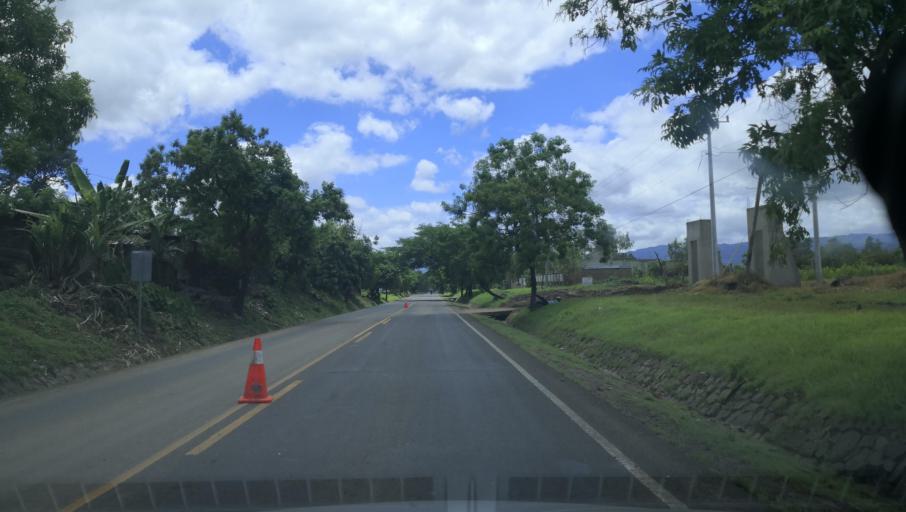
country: NI
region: Esteli
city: Esteli
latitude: 13.1641
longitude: -86.3684
